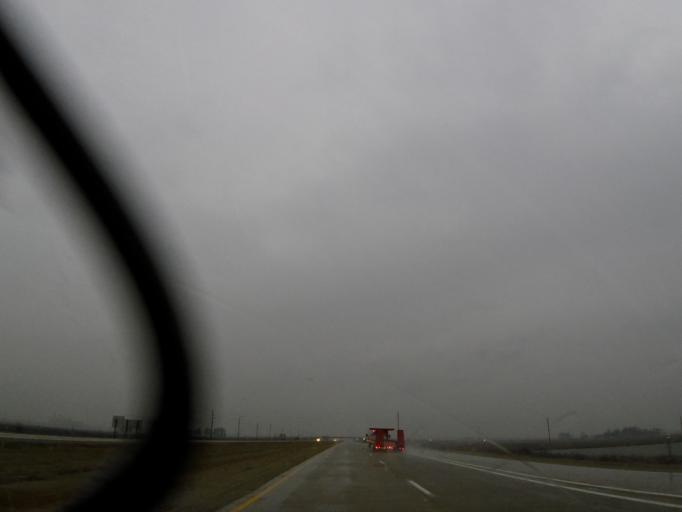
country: US
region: Iowa
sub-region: Cerro Gordo County
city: Mason City
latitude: 43.1055
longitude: -93.2669
